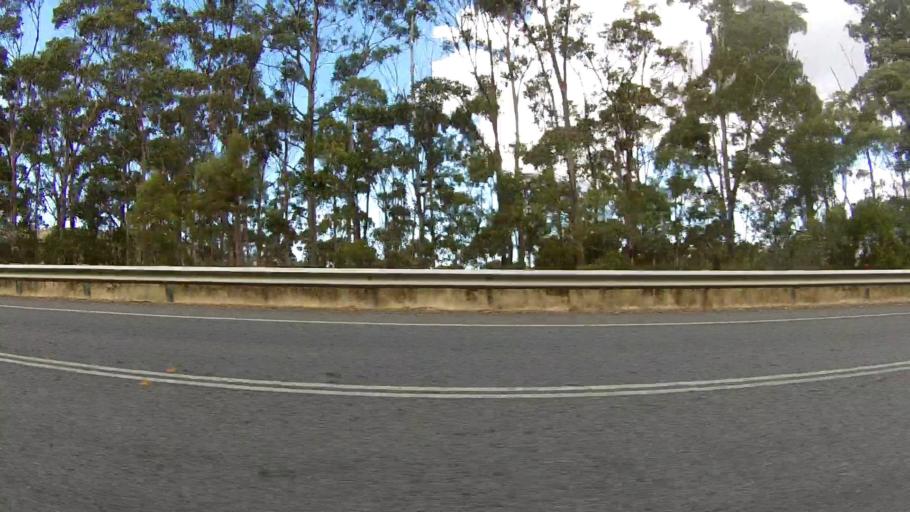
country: AU
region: Tasmania
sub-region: Sorell
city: Sorell
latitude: -42.6337
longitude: 147.6263
